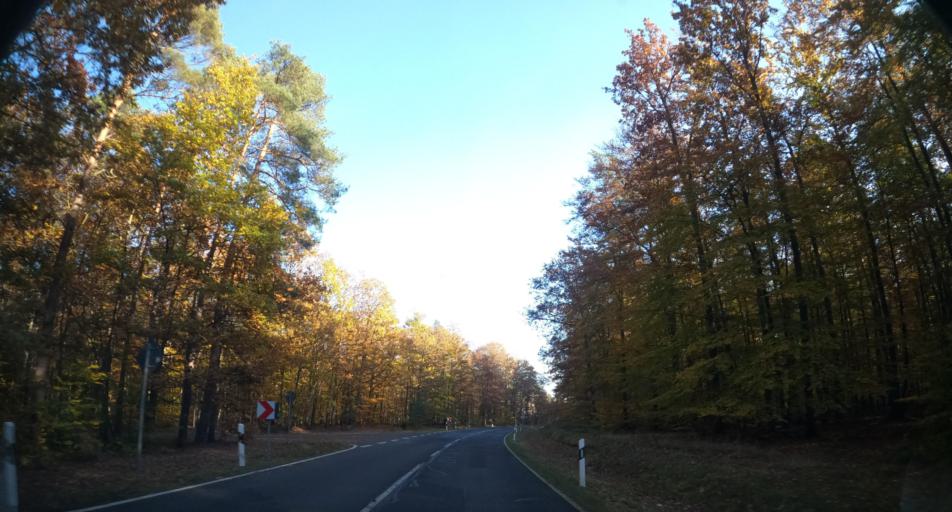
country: PL
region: West Pomeranian Voivodeship
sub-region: Powiat policki
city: Nowe Warpno
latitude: 53.6204
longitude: 14.2860
